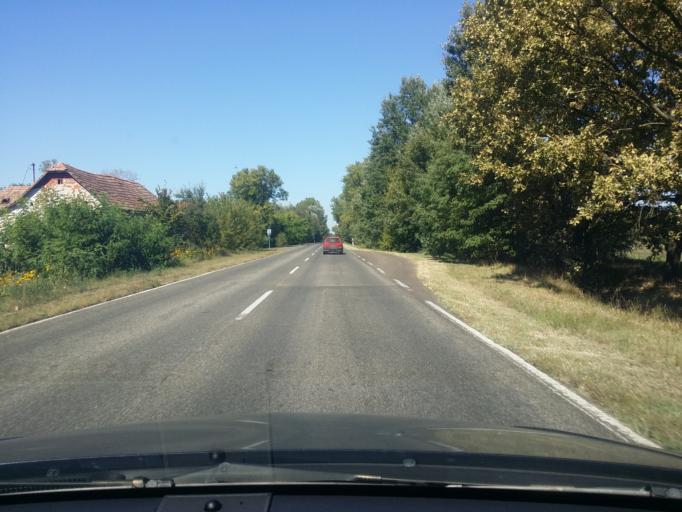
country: HU
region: Csongrad
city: Pusztaszer
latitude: 46.5505
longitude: 19.9501
